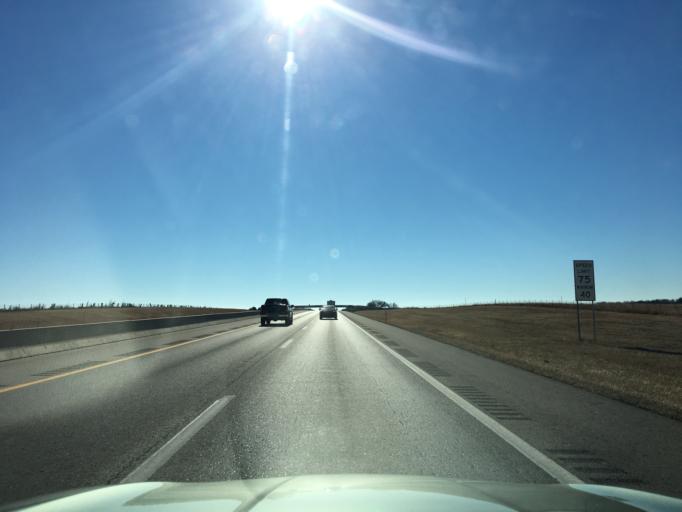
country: US
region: Kansas
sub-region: Sumner County
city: Wellington
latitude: 37.0474
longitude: -97.3384
